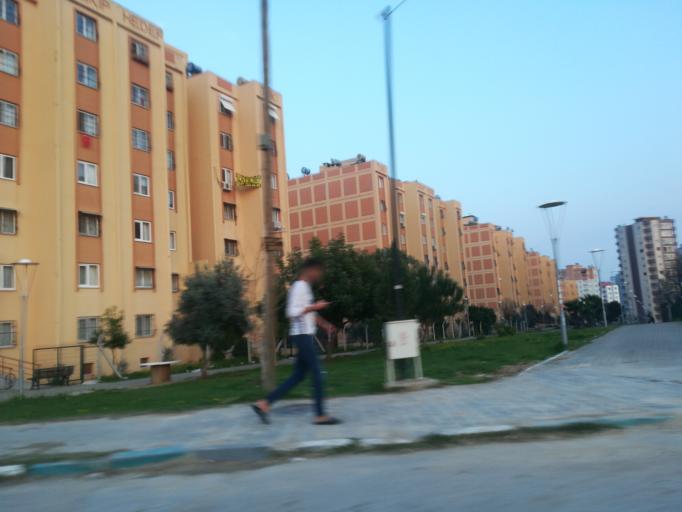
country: TR
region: Adana
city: Adana
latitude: 37.0740
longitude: 35.4081
